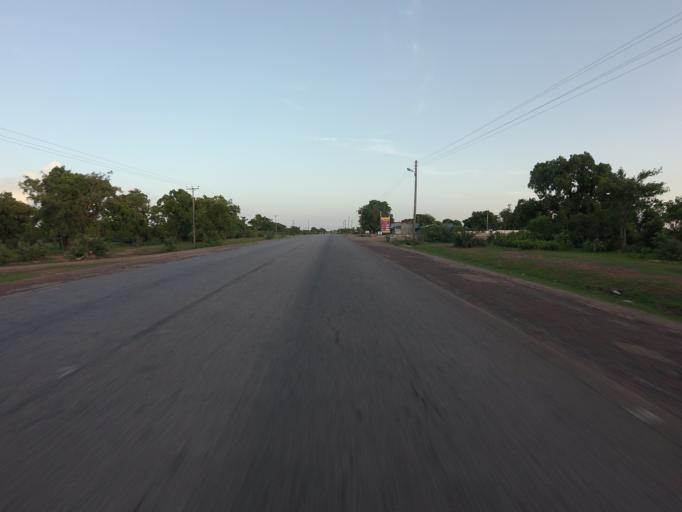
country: GH
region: Upper East
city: Navrongo
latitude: 10.9465
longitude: -1.0939
